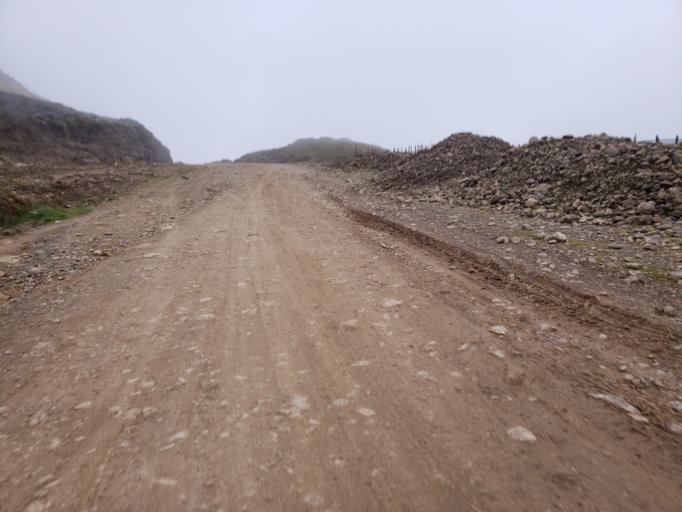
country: ET
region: Oromiya
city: Dodola
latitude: 6.7275
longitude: 39.4284
